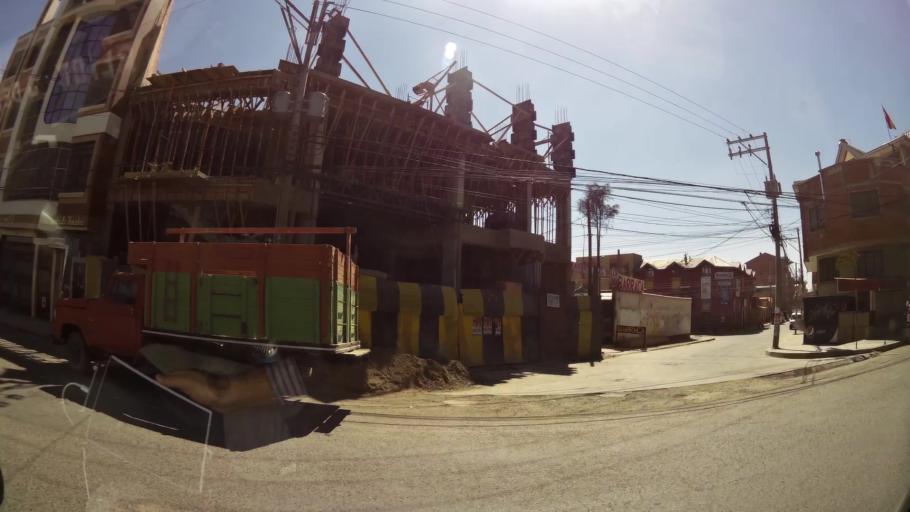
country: BO
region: La Paz
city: La Paz
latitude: -16.5002
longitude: -68.1735
